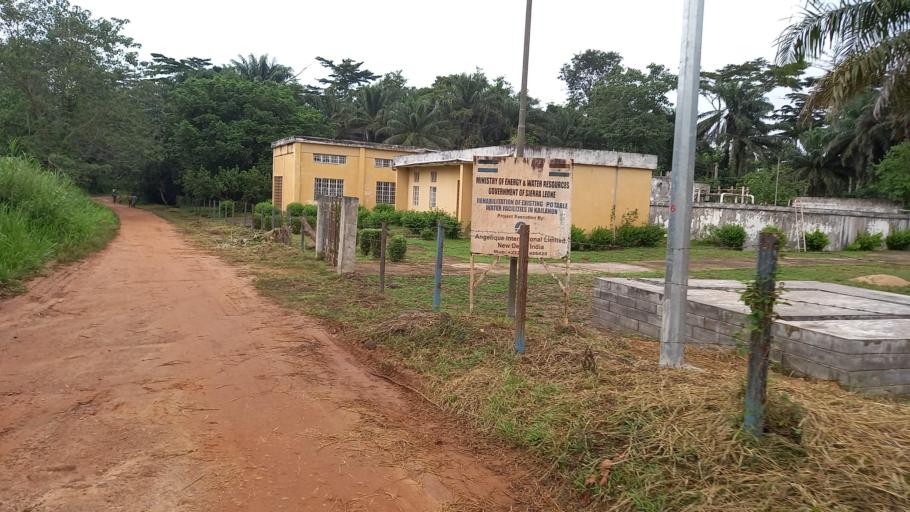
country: SL
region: Eastern Province
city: Kailahun
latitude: 8.2422
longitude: -10.5185
